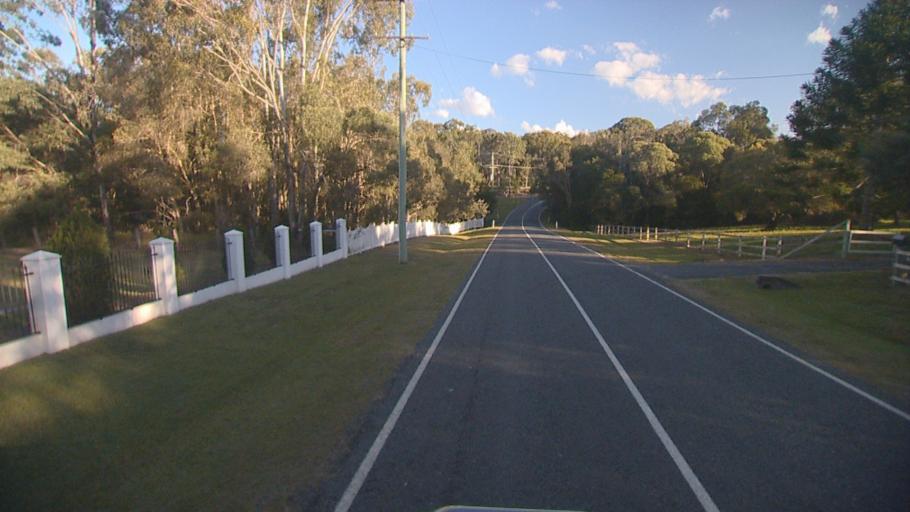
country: AU
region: Queensland
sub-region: Redland
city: Redland Bay
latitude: -27.6634
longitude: 153.2768
